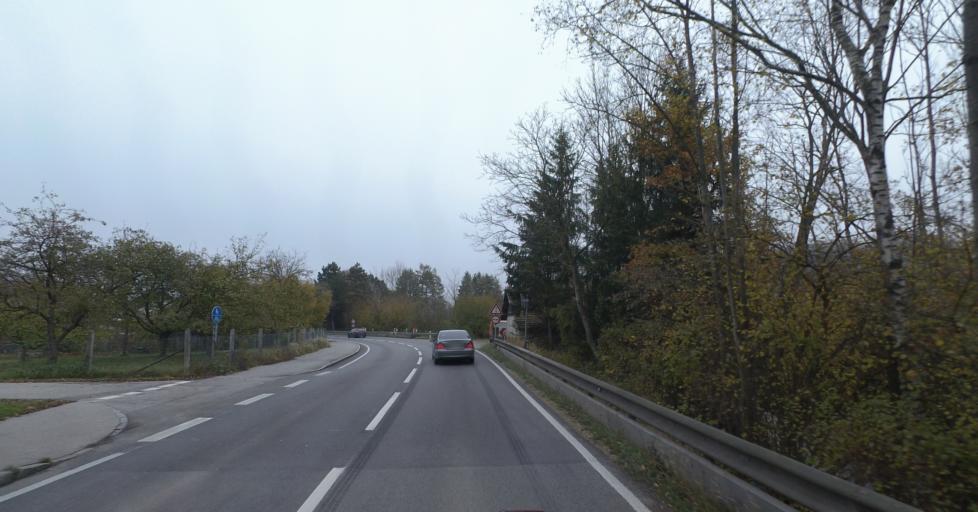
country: DE
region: Bavaria
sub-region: Upper Bavaria
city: Garching an der Alz
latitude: 48.1203
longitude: 12.5746
